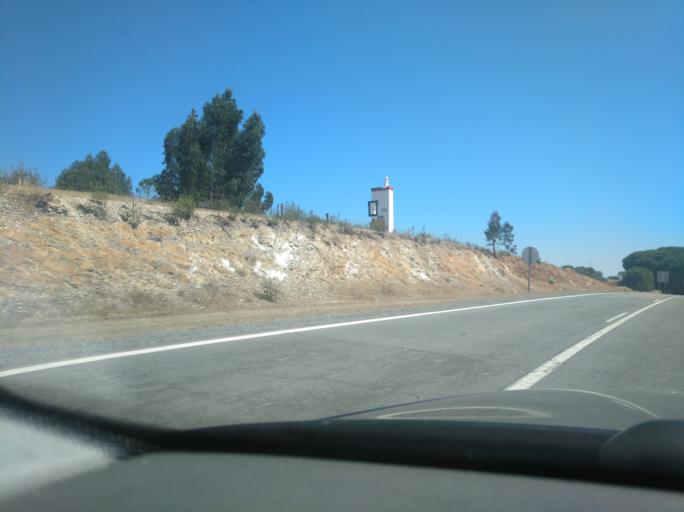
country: PT
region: Beja
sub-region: Castro Verde
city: Castro Verde
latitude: 37.6174
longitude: -8.0826
